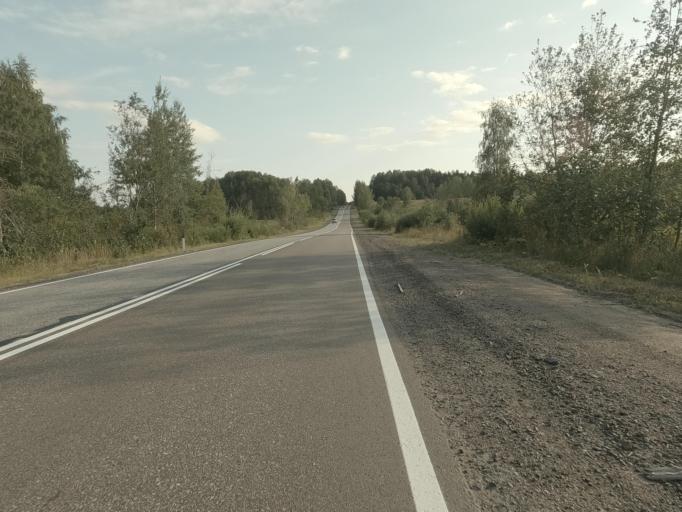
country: RU
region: Leningrad
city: Vyborg
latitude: 60.8392
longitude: 28.8399
